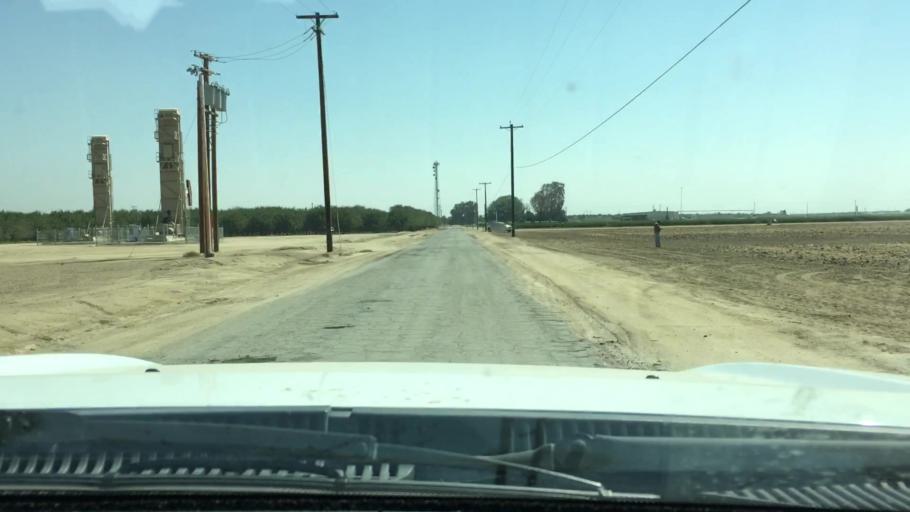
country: US
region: California
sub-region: Kern County
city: Shafter
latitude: 35.5364
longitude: -119.2755
